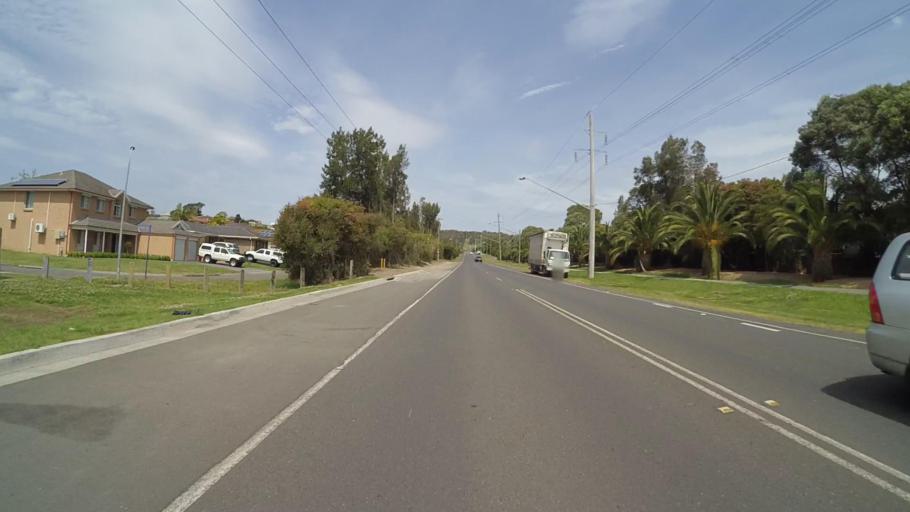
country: AU
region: New South Wales
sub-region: Shellharbour
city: Albion Park Rail
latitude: -34.5863
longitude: 150.7796
